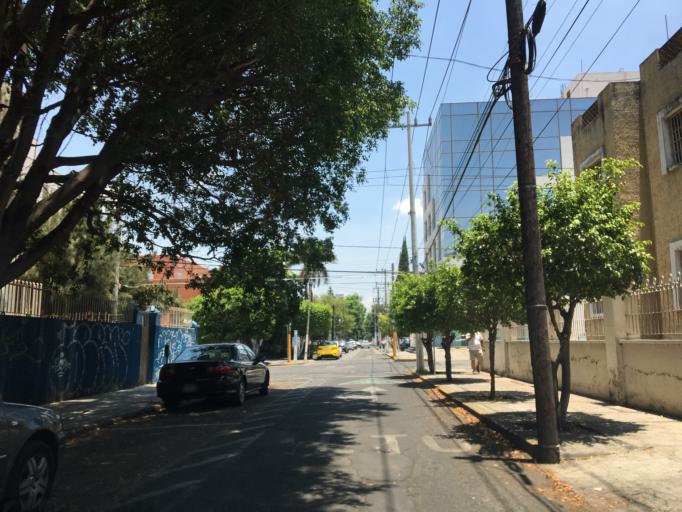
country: MX
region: Jalisco
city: Guadalajara
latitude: 20.6758
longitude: -103.3717
